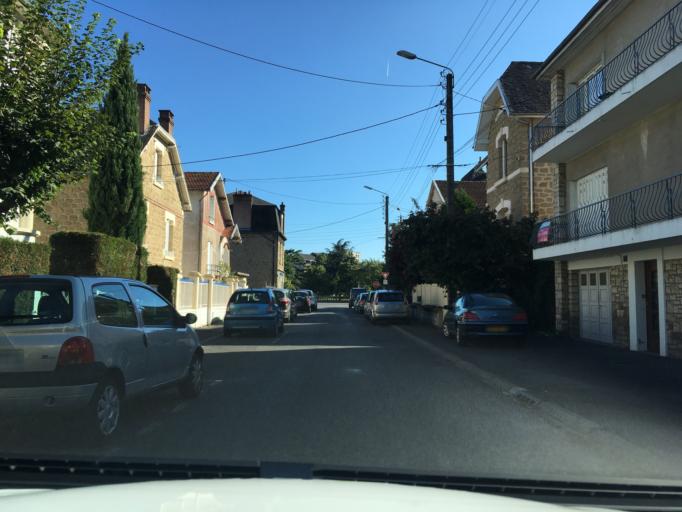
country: FR
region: Limousin
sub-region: Departement de la Correze
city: Brive-la-Gaillarde
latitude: 45.1660
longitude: 1.5352
